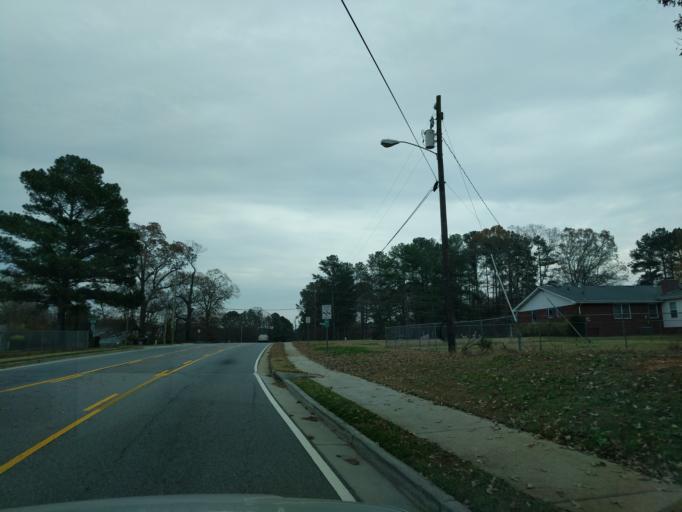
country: US
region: Georgia
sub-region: Gwinnett County
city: Duluth
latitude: 34.0188
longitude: -84.1578
